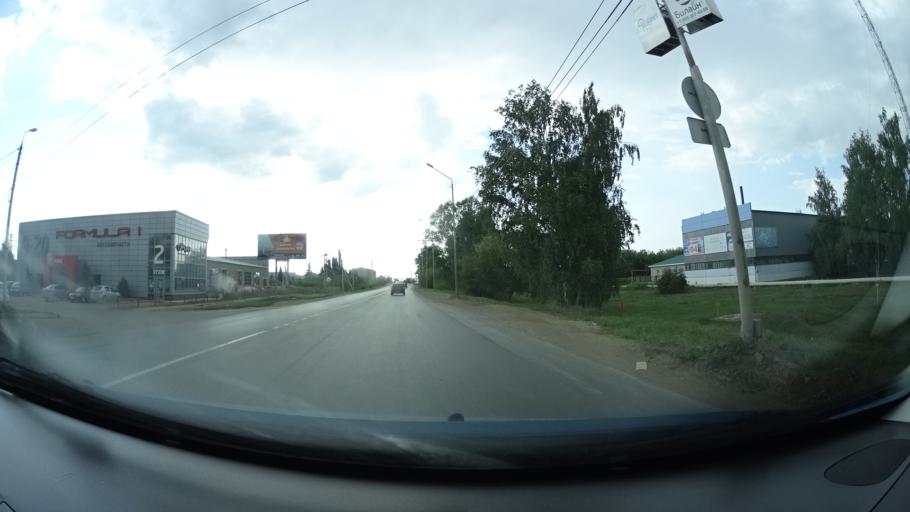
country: RU
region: Bashkortostan
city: Oktyabr'skiy
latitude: 54.4925
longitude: 53.4528
